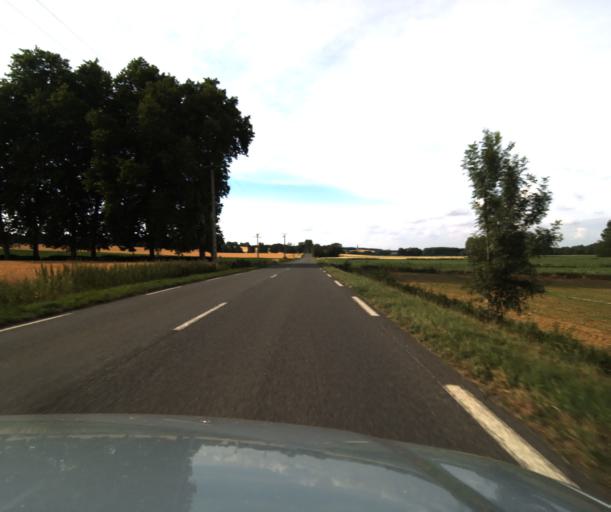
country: FR
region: Midi-Pyrenees
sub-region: Departement du Tarn-et-Garonne
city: Beaumont-de-Lomagne
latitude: 43.7920
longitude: 0.8943
